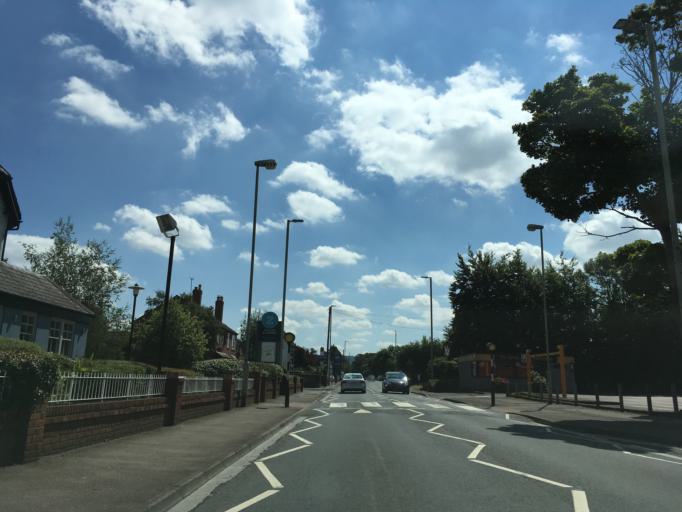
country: GB
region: England
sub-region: Gloucestershire
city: Barnwood
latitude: 51.8557
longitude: -2.1884
